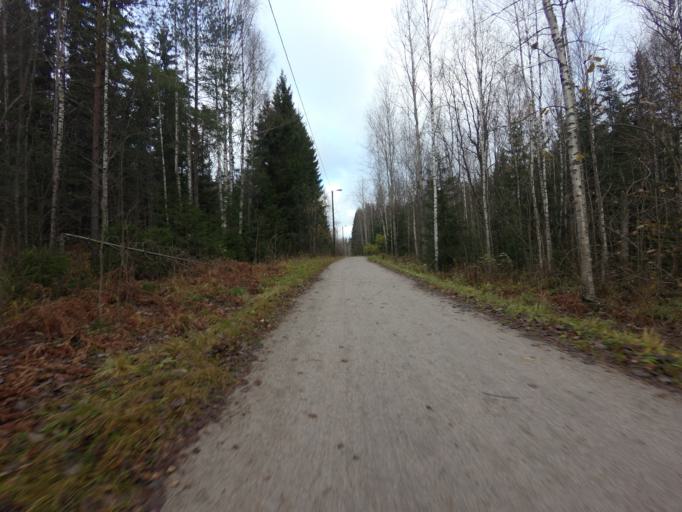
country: FI
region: Uusimaa
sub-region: Helsinki
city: Kauniainen
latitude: 60.1943
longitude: 24.6984
